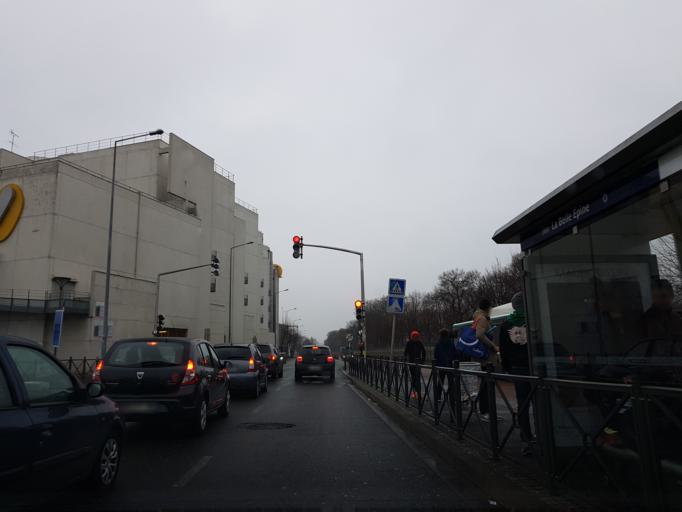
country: FR
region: Ile-de-France
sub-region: Departement du Val-de-Marne
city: Orly
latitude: 48.7562
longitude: 2.3743
